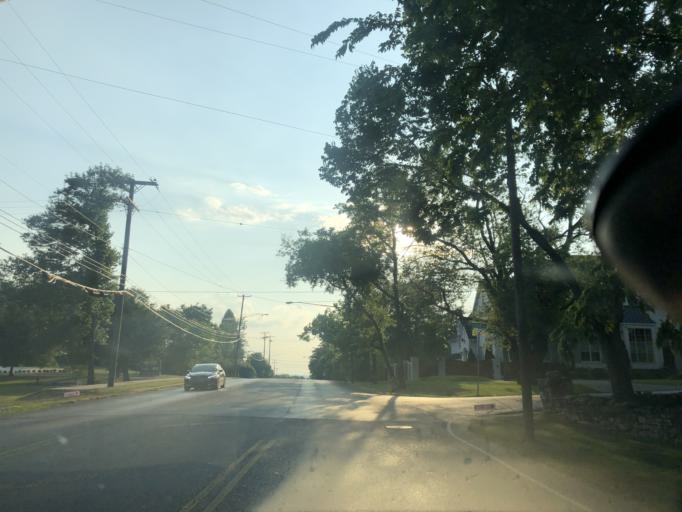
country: US
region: Tennessee
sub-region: Davidson County
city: Oak Hill
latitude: 36.1137
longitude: -86.8073
